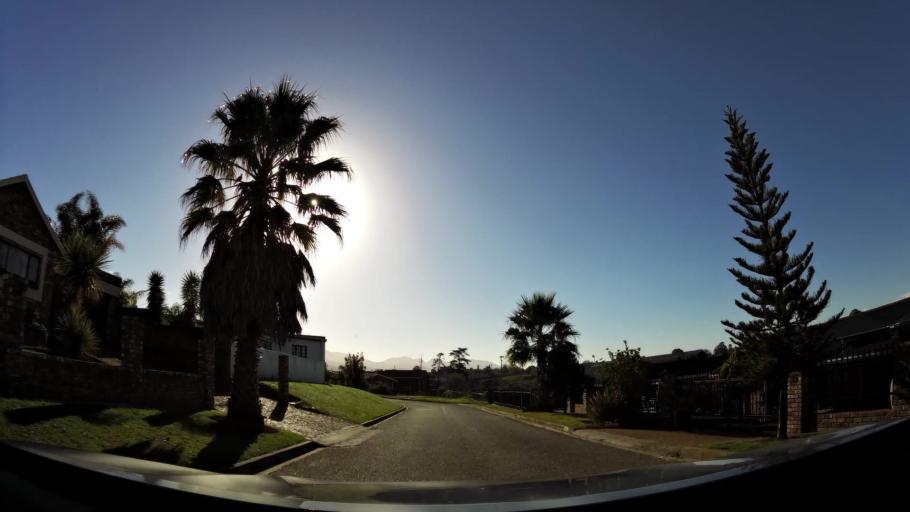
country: ZA
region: Western Cape
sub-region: Eden District Municipality
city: George
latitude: -33.9720
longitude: 22.4395
